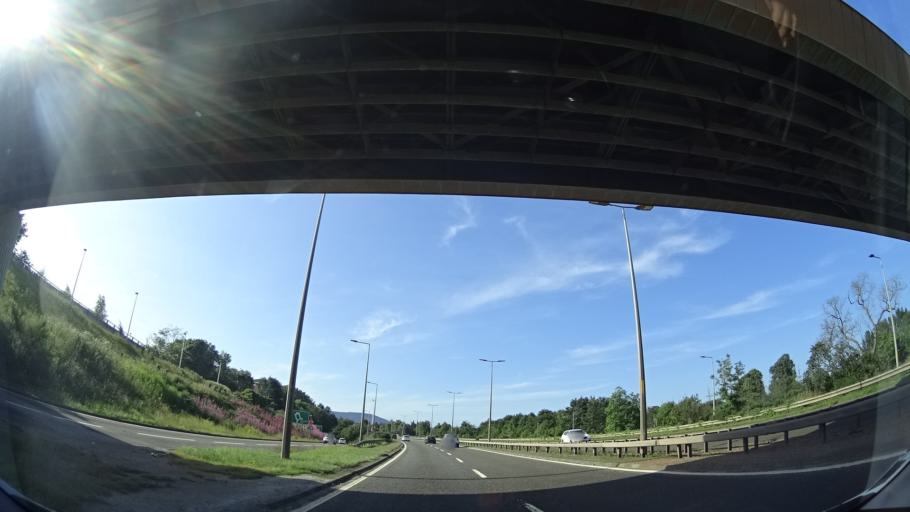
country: GB
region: Scotland
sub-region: Highland
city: Inverness
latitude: 57.4794
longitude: -4.1894
